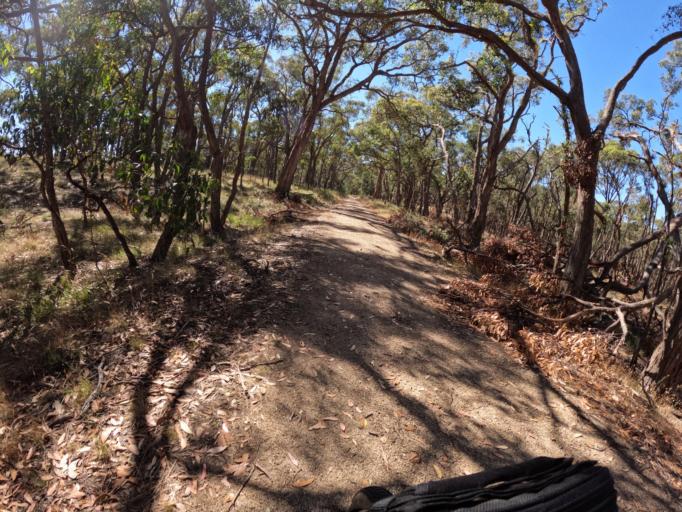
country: AU
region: Victoria
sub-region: Ballarat North
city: Delacombe
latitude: -37.6670
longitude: 143.5132
